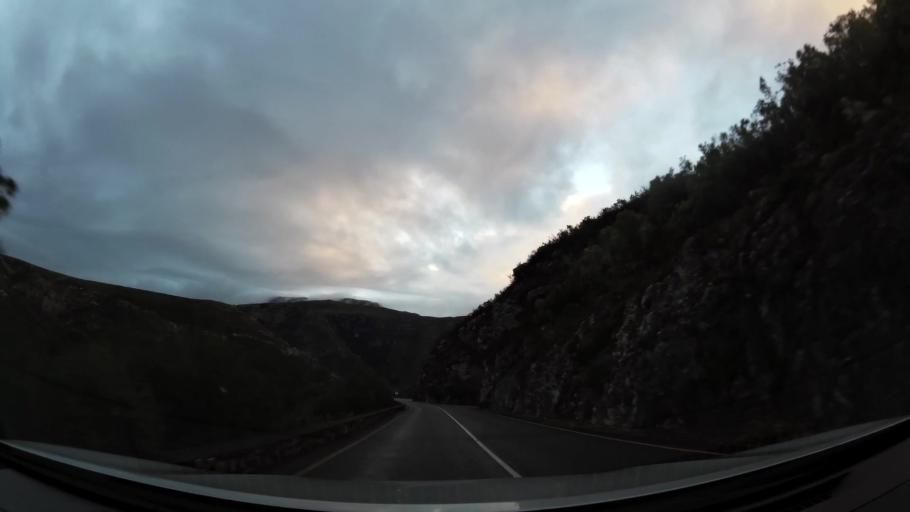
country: ZA
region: Western Cape
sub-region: Overberg District Municipality
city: Swellendam
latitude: -33.9834
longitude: 20.7098
